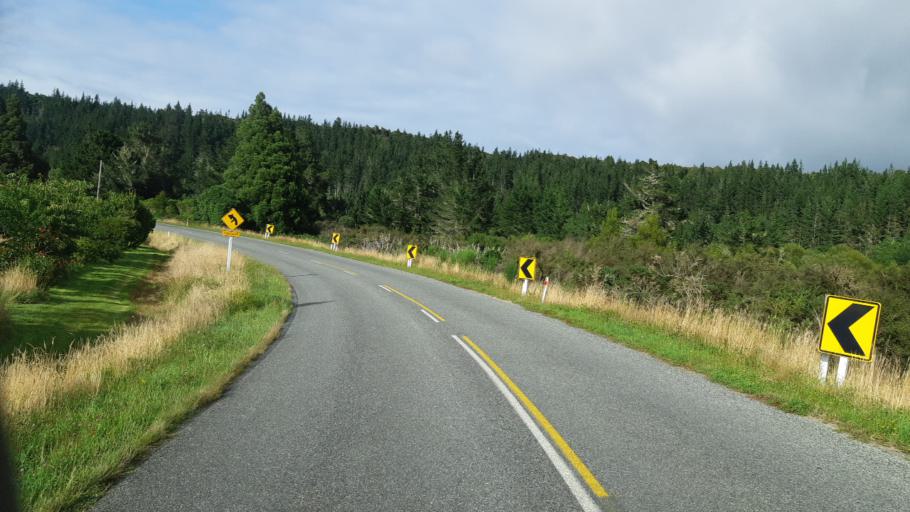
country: NZ
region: West Coast
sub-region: Westland District
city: Hokitika
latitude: -42.7468
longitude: 170.9973
